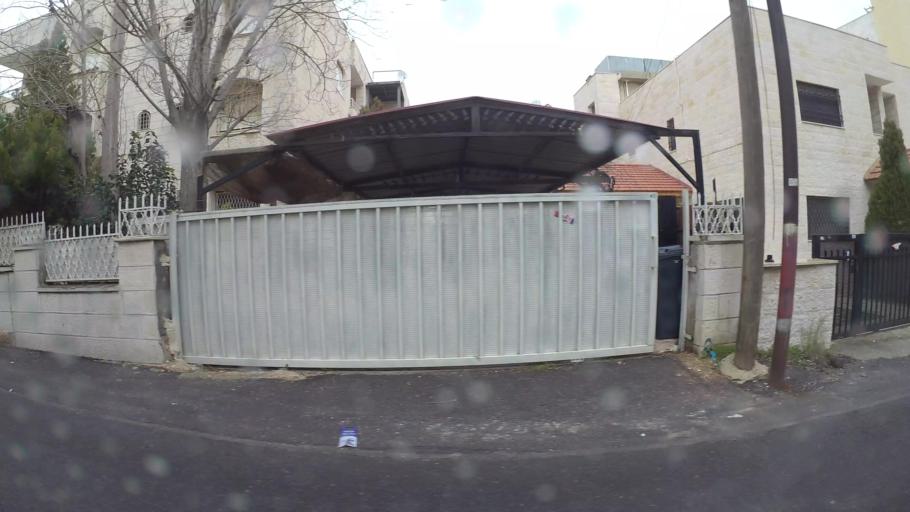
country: JO
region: Amman
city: Al Jubayhah
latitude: 31.9873
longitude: 35.8614
